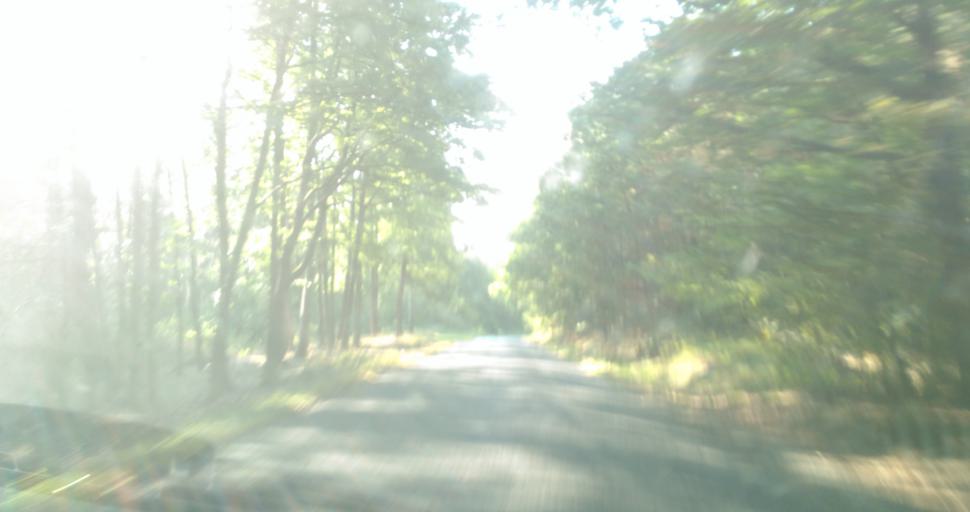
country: CZ
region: Central Bohemia
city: Roztoky
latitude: 49.9788
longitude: 13.8686
